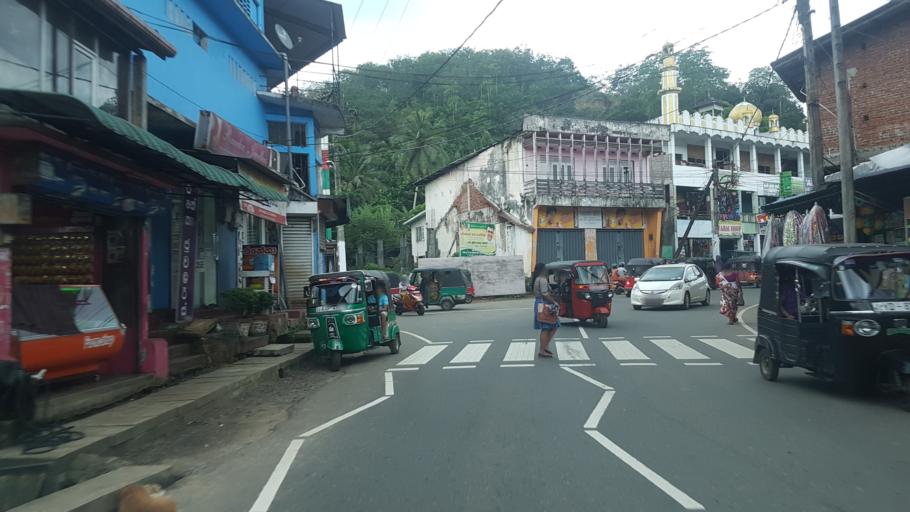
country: LK
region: Western
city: Hanwella Ihala
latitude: 7.0298
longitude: 80.2958
